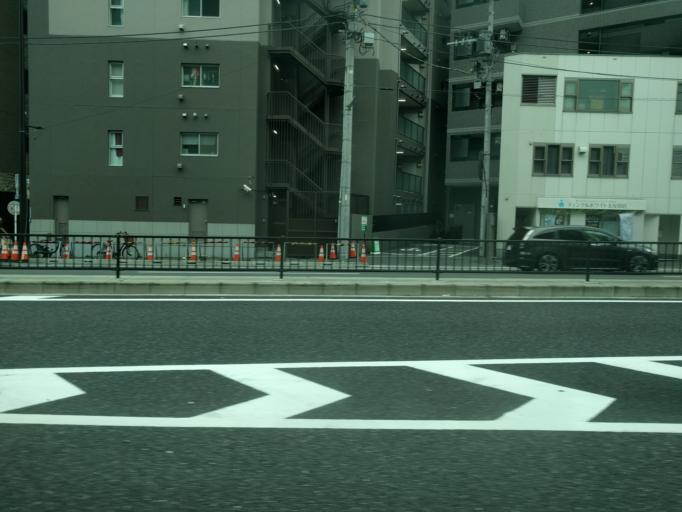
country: JP
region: Tokyo
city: Tokyo
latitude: 35.6279
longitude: 139.7126
